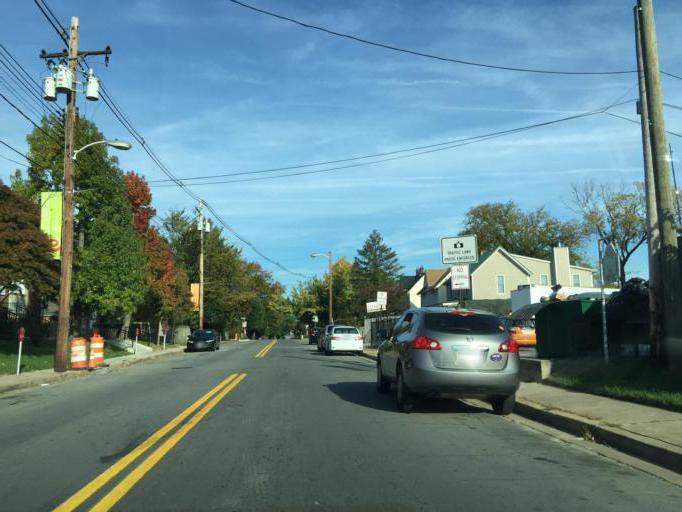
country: US
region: Maryland
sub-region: Baltimore County
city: Towson
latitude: 39.3594
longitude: -76.6107
